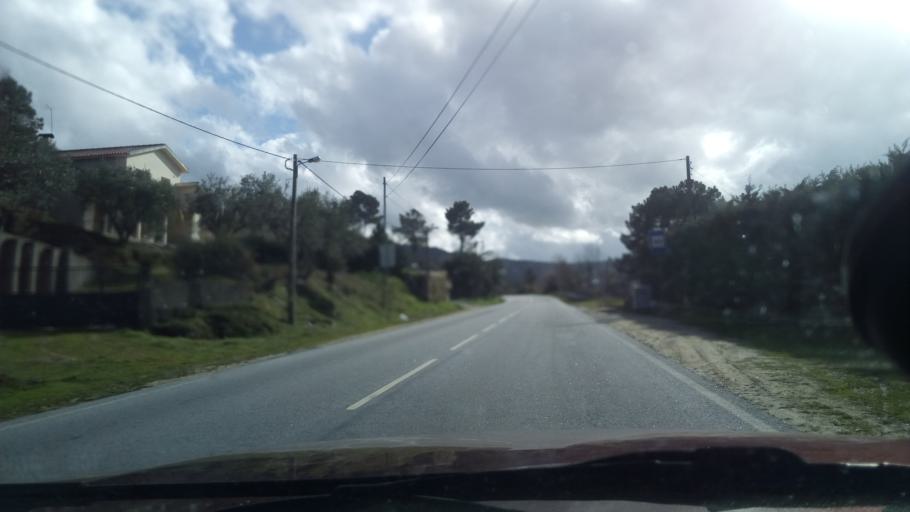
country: PT
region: Guarda
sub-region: Guarda
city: Guarda
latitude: 40.5760
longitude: -7.2964
